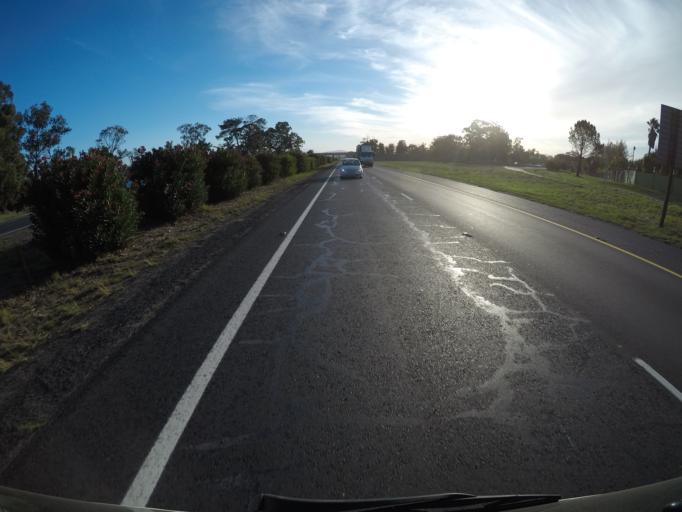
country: ZA
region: Western Cape
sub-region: City of Cape Town
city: Kraaifontein
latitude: -33.8346
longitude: 18.7384
